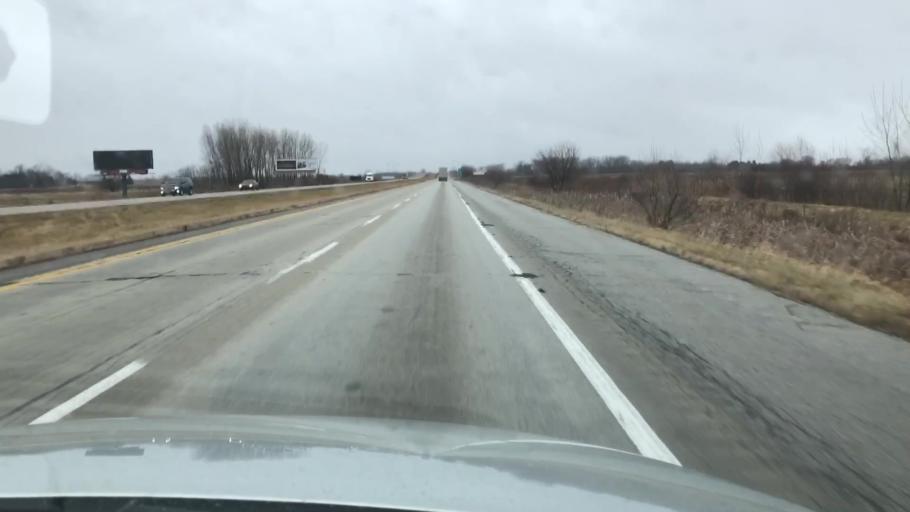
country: US
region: Indiana
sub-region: Starke County
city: Knox
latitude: 41.3941
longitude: -86.6080
